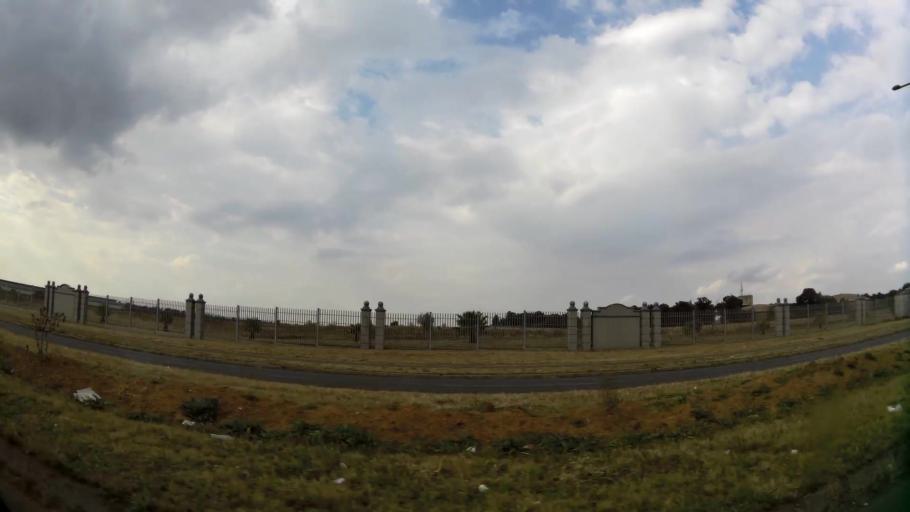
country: ZA
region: Gauteng
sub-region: Sedibeng District Municipality
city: Vanderbijlpark
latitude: -26.6839
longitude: 27.8203
